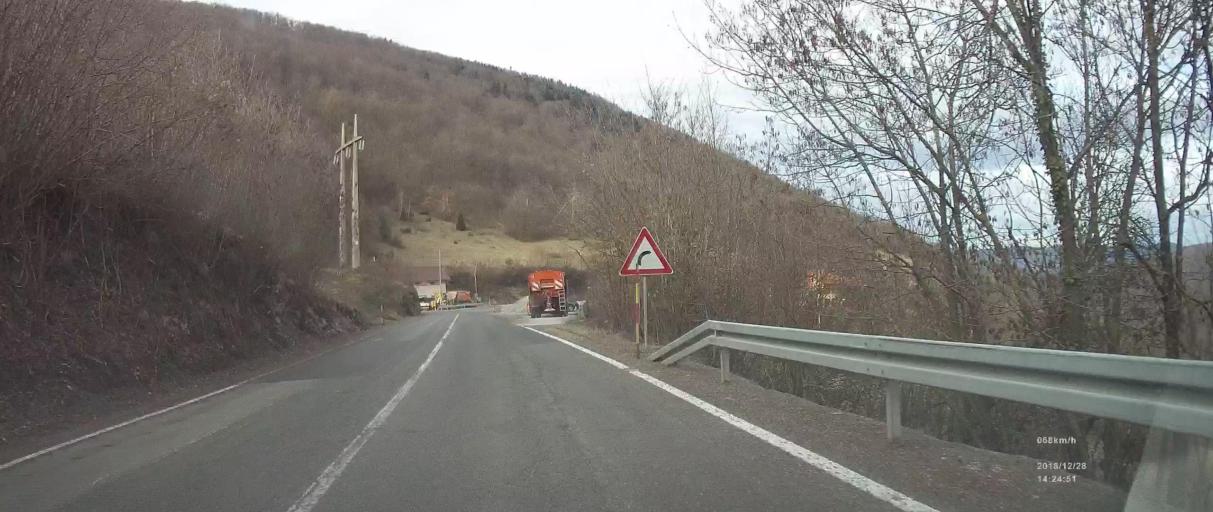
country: HR
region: Primorsko-Goranska
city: Vrbovsko
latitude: 45.3888
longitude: 15.1052
